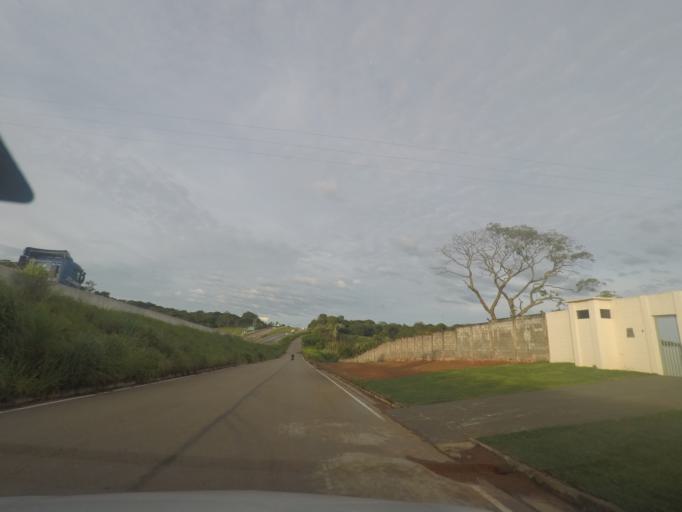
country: BR
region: Goias
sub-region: Trindade
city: Trindade
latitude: -16.7351
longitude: -49.4027
